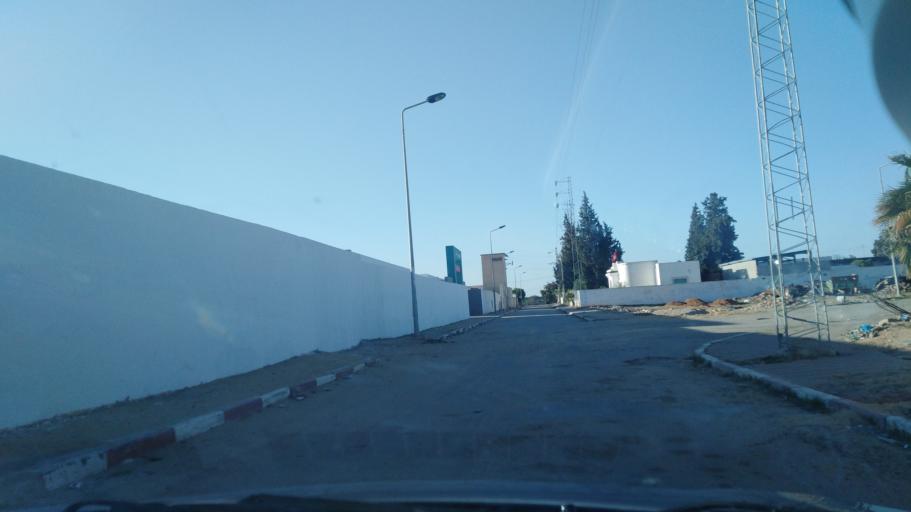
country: TN
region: Al Mahdiyah
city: Shurban
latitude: 34.9648
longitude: 10.3691
